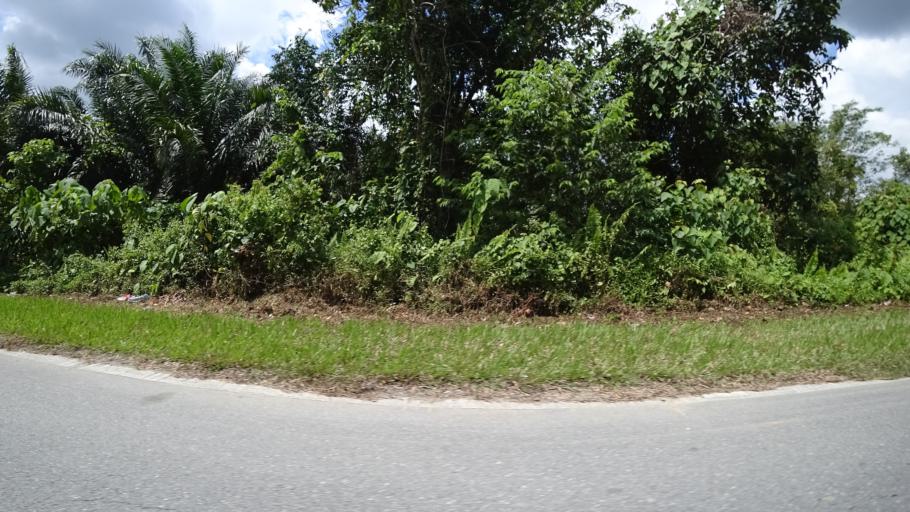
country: BN
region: Tutong
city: Tutong
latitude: 4.7189
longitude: 114.7999
